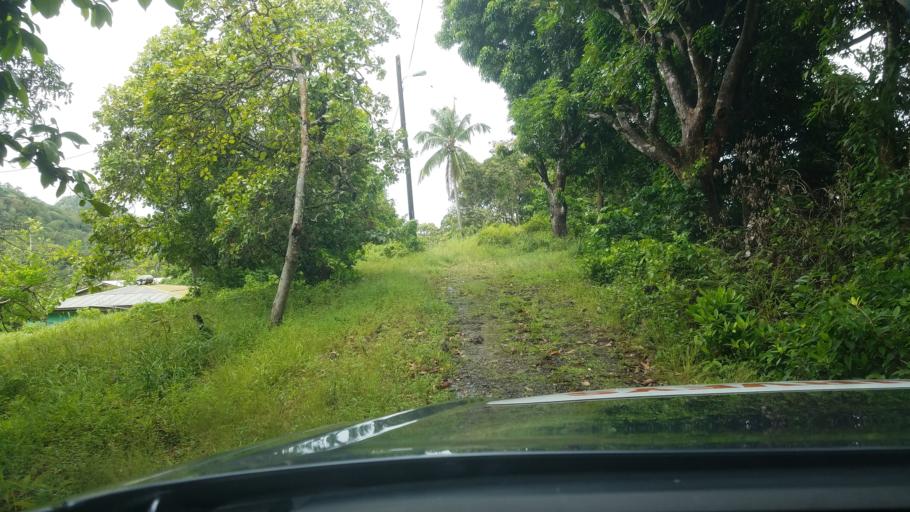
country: LC
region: Castries Quarter
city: Bisee
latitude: 13.9945
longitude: -60.9590
